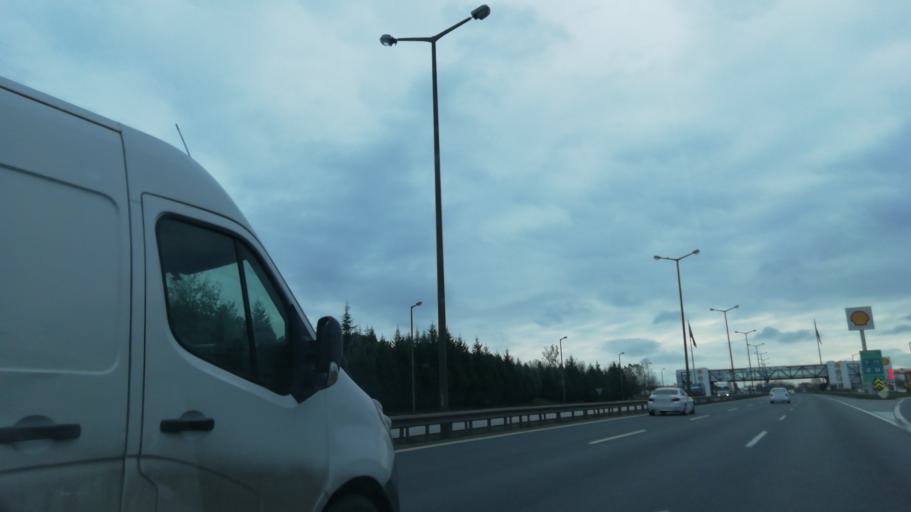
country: TR
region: Kocaeli
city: Derbent
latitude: 40.7284
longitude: 30.0666
